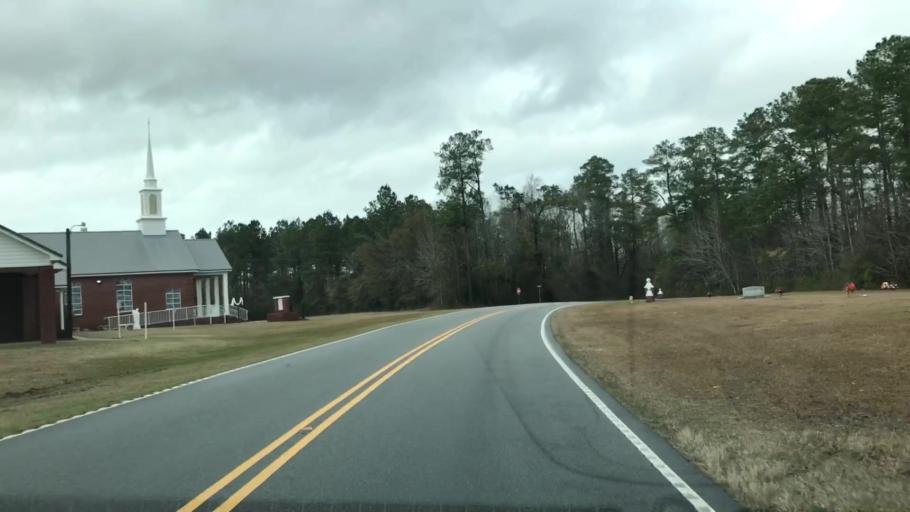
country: US
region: South Carolina
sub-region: Florence County
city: Johnsonville
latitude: 33.6555
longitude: -79.3044
